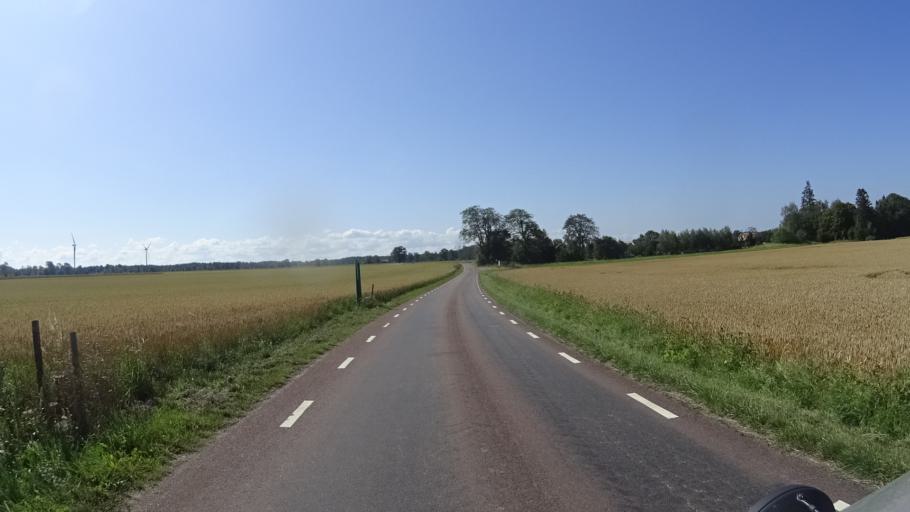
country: SE
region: OEstergoetland
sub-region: Vadstena Kommun
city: Herrestad
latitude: 58.3113
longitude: 14.8439
